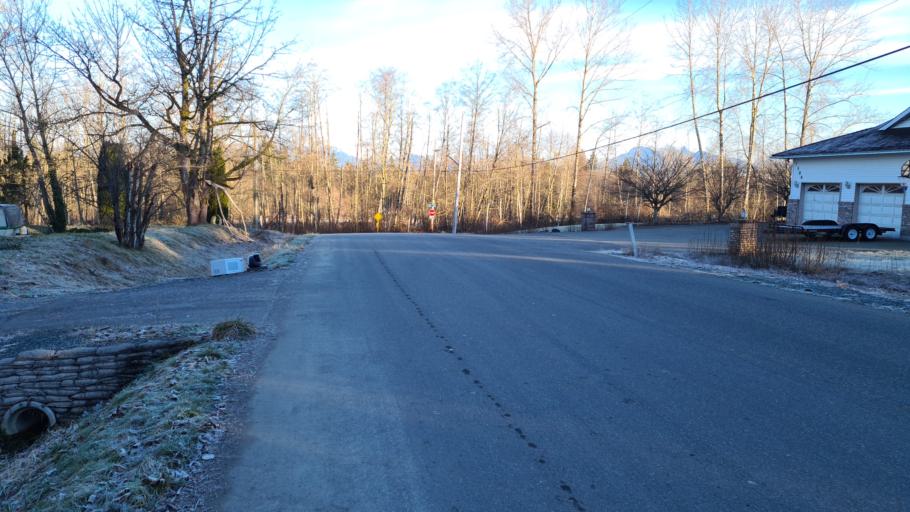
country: CA
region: British Columbia
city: Walnut Grove
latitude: 49.1402
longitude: -122.6723
